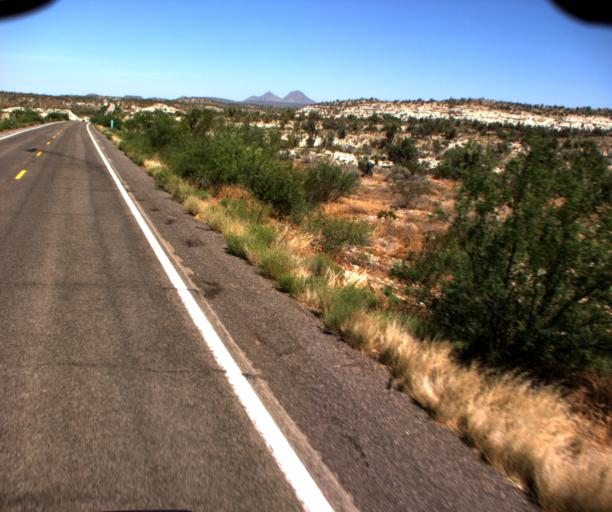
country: US
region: Arizona
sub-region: Graham County
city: Bylas
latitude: 33.2460
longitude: -110.2683
